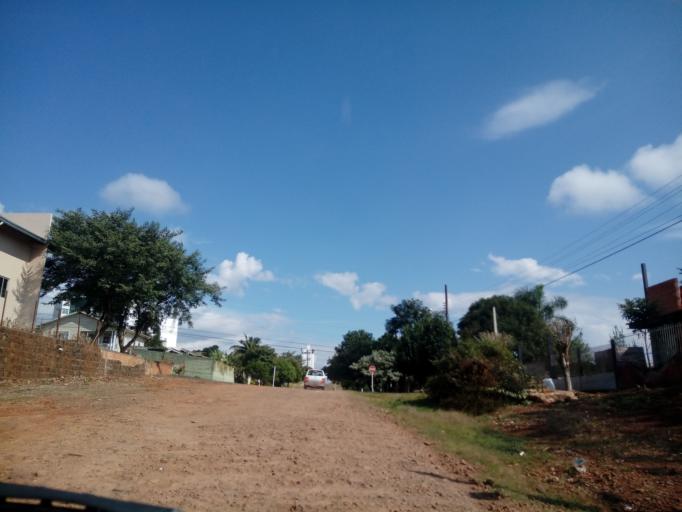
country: BR
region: Santa Catarina
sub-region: Chapeco
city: Chapeco
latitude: -27.0997
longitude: -52.6000
